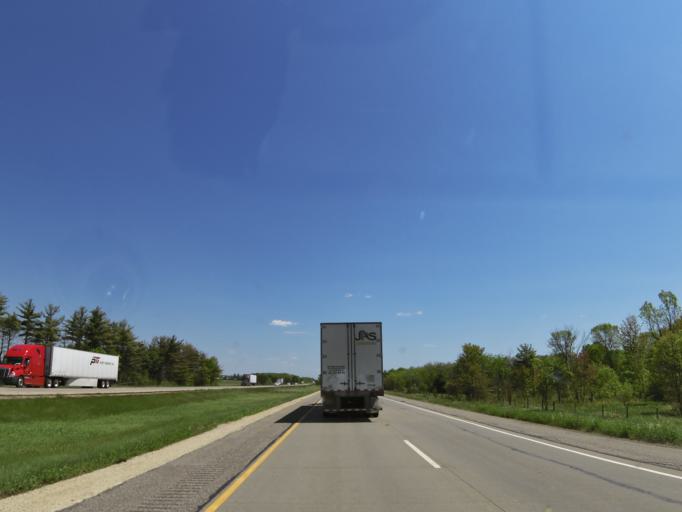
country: US
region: Wisconsin
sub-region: Juneau County
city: New Lisbon
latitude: 43.9044
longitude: -90.2070
